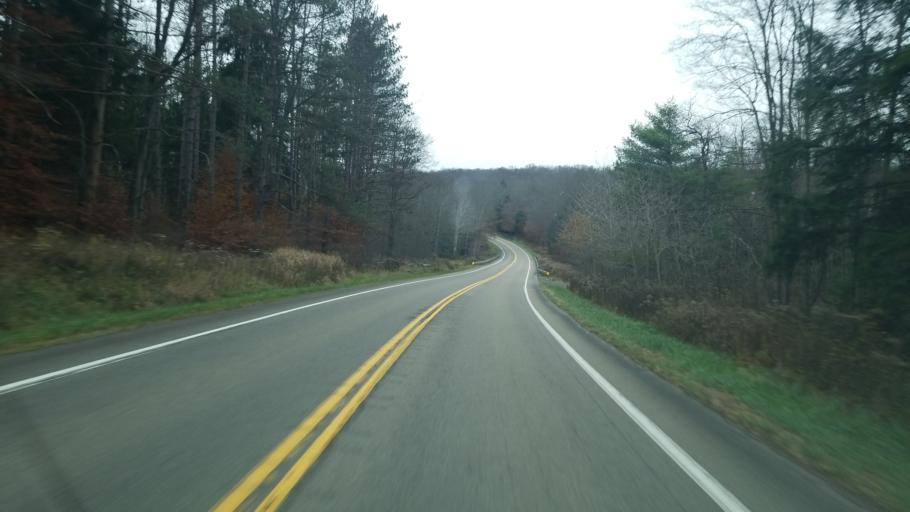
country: US
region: Pennsylvania
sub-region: Forest County
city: Marienville
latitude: 41.5501
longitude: -79.0161
